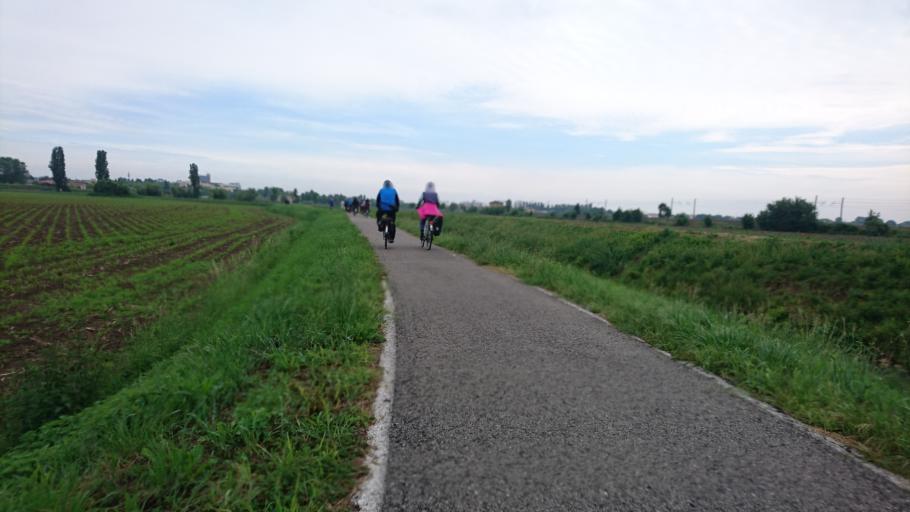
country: IT
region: Veneto
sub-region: Provincia di Padova
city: Montegrotto Terme
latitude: 45.3163
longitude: 11.7888
